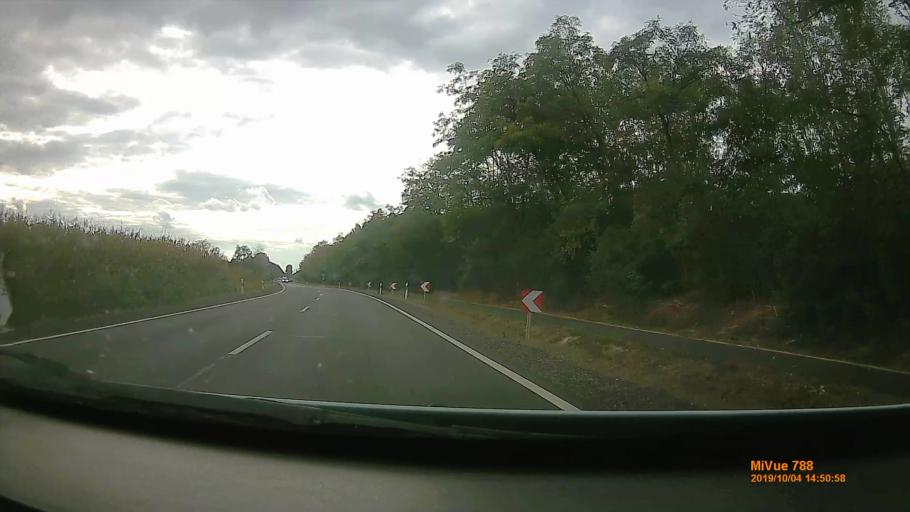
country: HU
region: Szabolcs-Szatmar-Bereg
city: Nyirpazony
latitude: 47.9773
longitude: 21.7703
